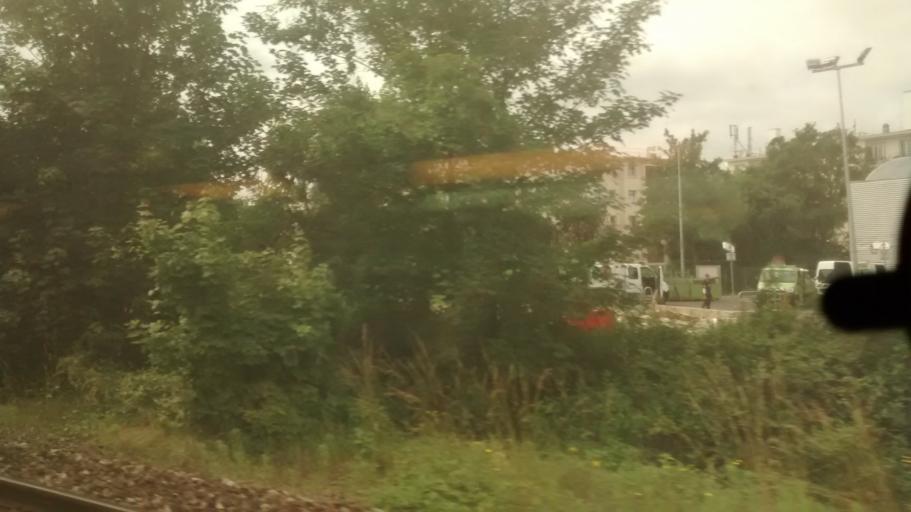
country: FR
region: Ile-de-France
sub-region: Departement du Val-de-Marne
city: Villeneuve-le-Roi
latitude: 48.7444
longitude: 2.3996
